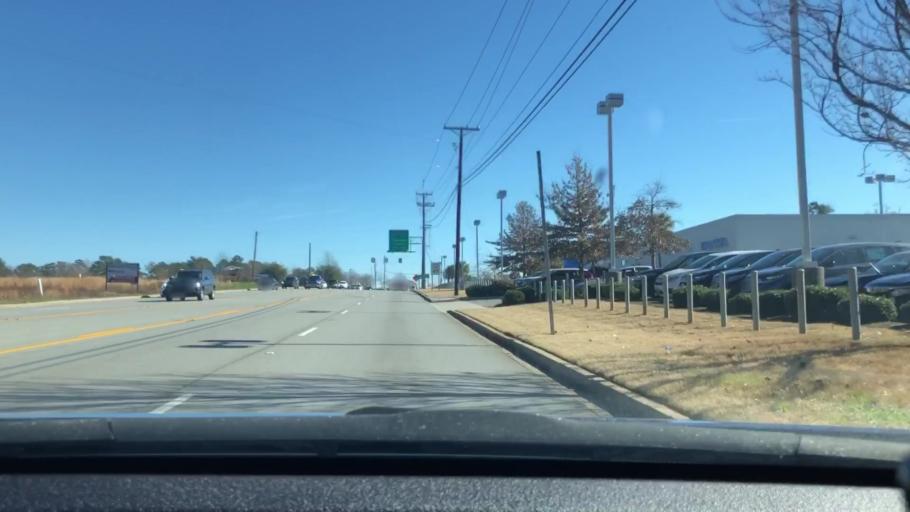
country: US
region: South Carolina
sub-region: Lexington County
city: Oak Grove
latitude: 34.0139
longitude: -81.1567
